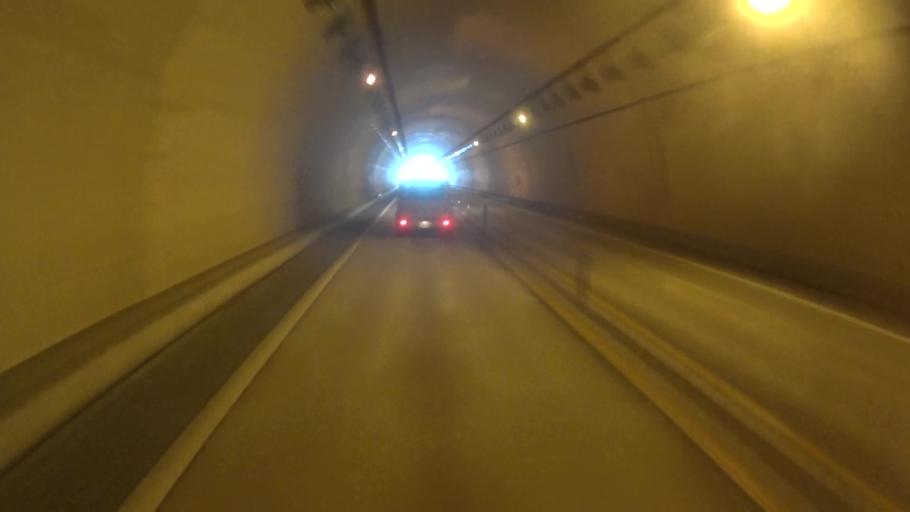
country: JP
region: Kyoto
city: Miyazu
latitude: 35.4596
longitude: 135.1754
